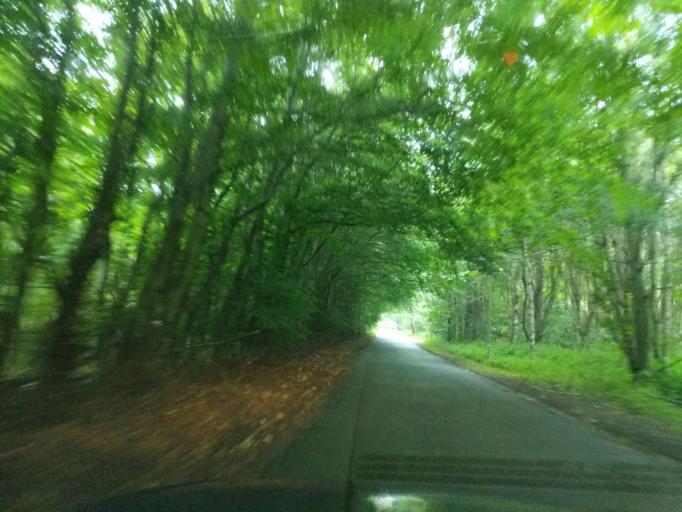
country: GB
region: Scotland
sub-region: Aberdeenshire
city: Aboyne
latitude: 57.0745
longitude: -2.8037
